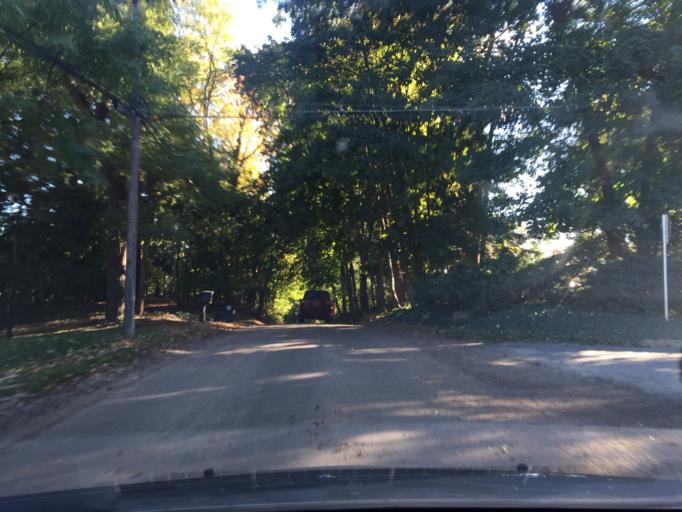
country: US
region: Michigan
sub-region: Oakland County
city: Franklin
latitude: 42.5573
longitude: -83.2952
